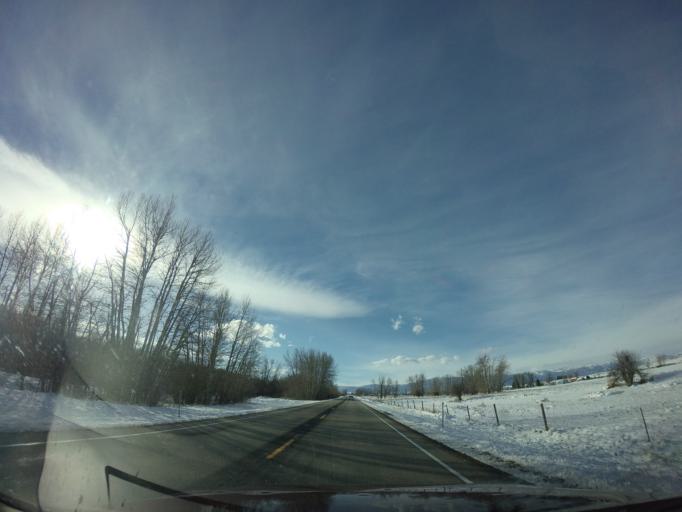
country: US
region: Montana
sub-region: Carbon County
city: Red Lodge
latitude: 45.3257
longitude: -109.1885
